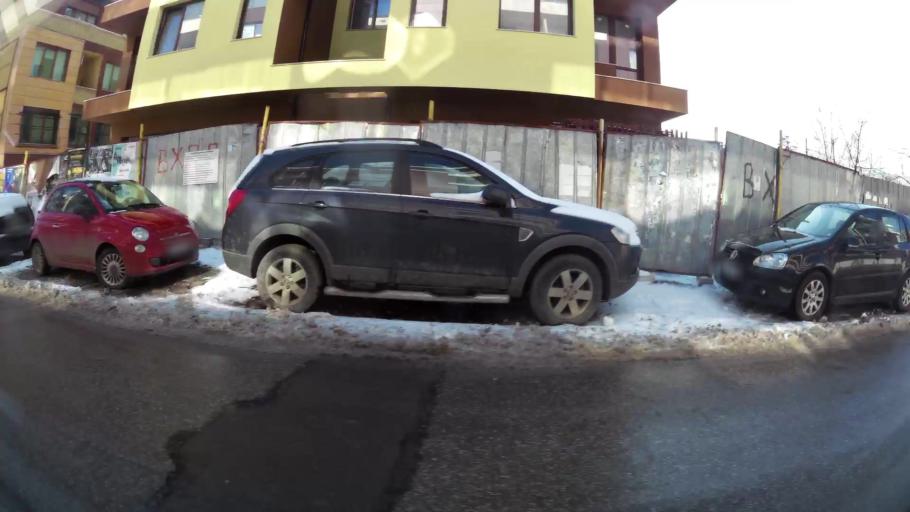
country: BG
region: Sofia-Capital
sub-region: Stolichna Obshtina
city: Sofia
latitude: 42.6537
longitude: 23.3320
